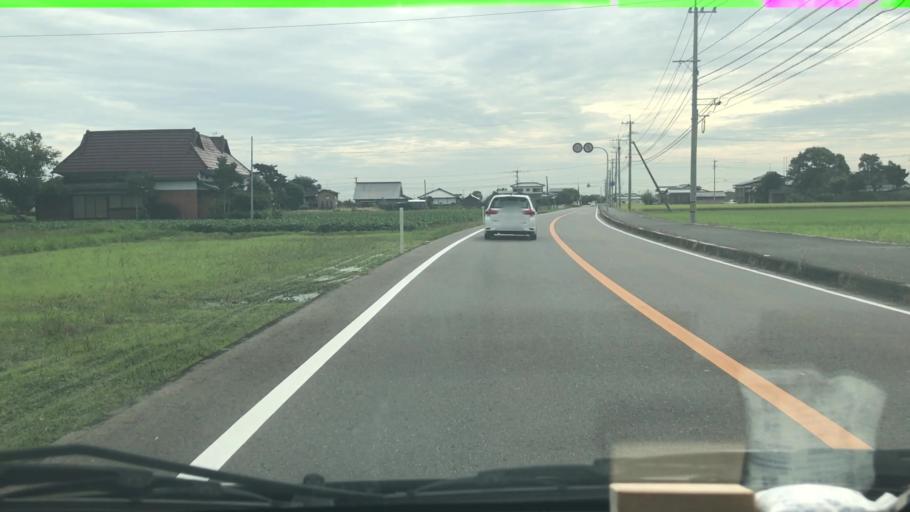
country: JP
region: Saga Prefecture
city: Takeocho-takeo
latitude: 33.1976
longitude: 130.1066
